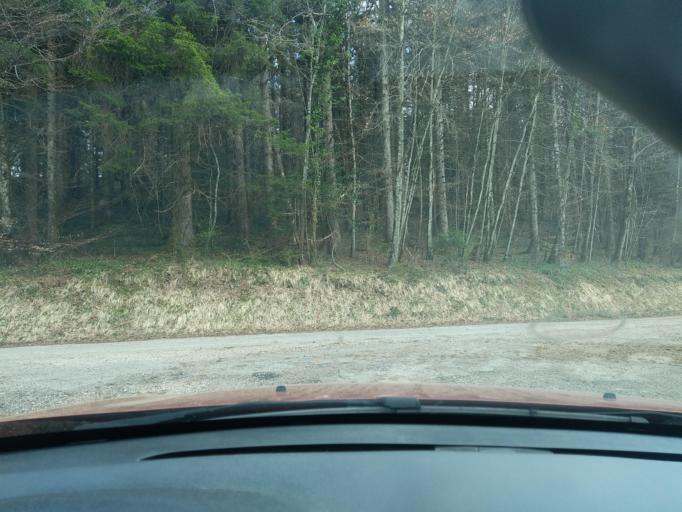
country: FR
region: Franche-Comte
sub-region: Departement du Jura
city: Moirans-en-Montagne
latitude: 46.4588
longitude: 5.7603
